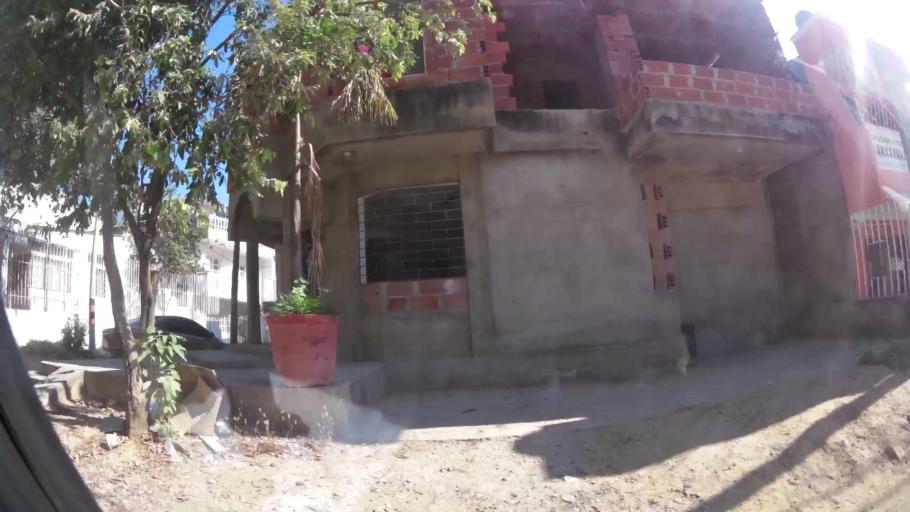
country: CO
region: Bolivar
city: Cartagena
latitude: 10.3934
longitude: -75.4750
